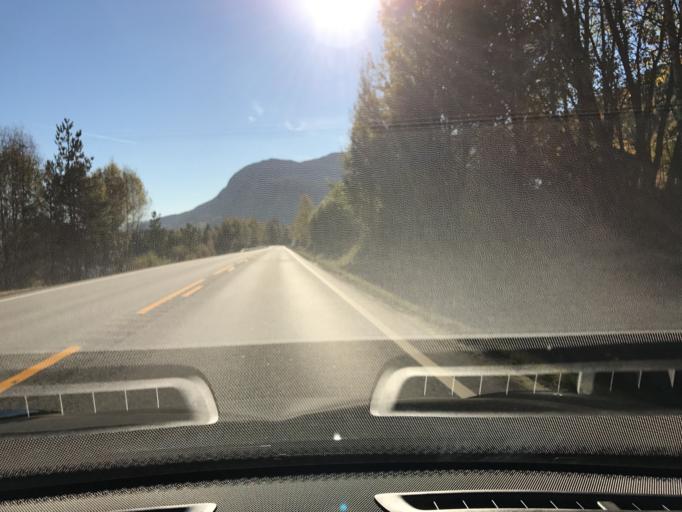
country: NO
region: Buskerud
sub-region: Nes
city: Nesbyen
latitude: 60.5879
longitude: 9.0880
